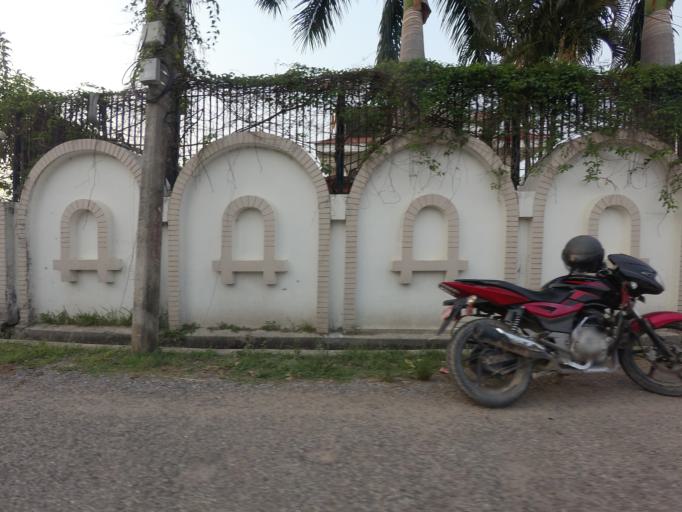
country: NP
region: Western Region
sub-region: Lumbini Zone
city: Bhairahawa
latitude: 27.5165
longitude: 83.4567
